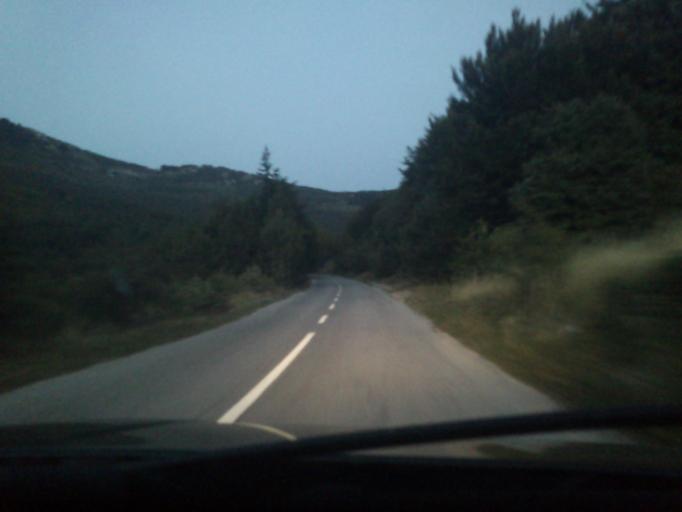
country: HR
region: Licko-Senjska
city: Senj
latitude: 44.8811
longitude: 14.9737
